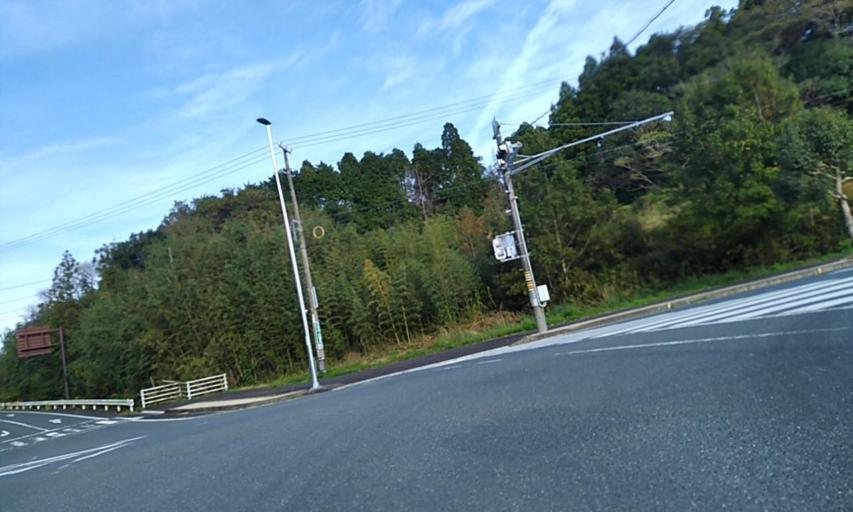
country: JP
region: Mie
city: Toba
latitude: 34.3693
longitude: 136.7929
